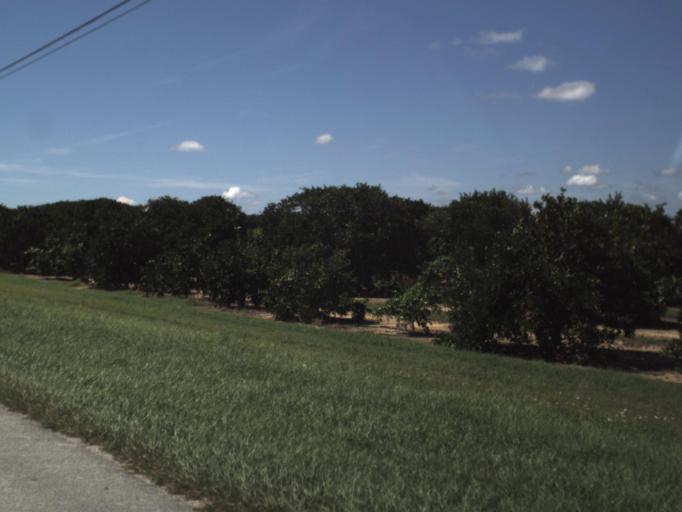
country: US
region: Florida
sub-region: Polk County
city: Lake Hamilton
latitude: 28.0670
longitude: -81.6200
